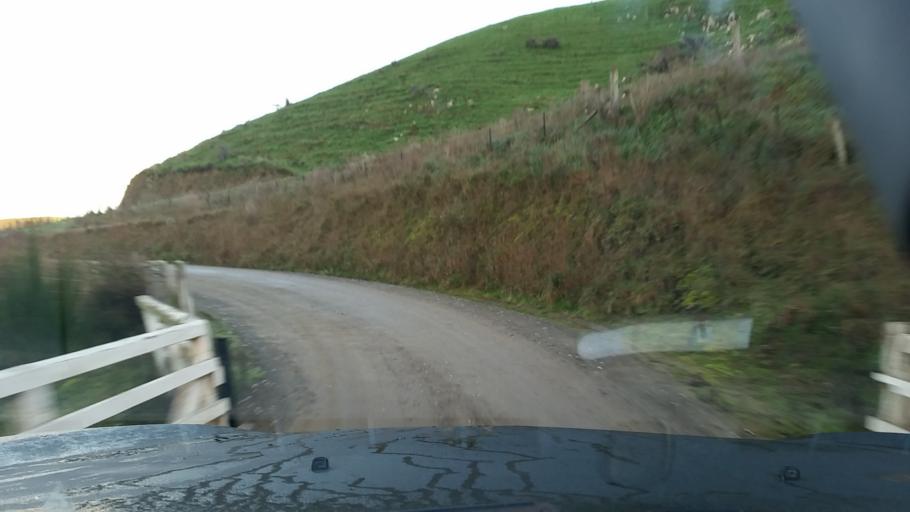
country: NZ
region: Marlborough
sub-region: Marlborough District
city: Blenheim
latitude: -41.5753
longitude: 173.9452
